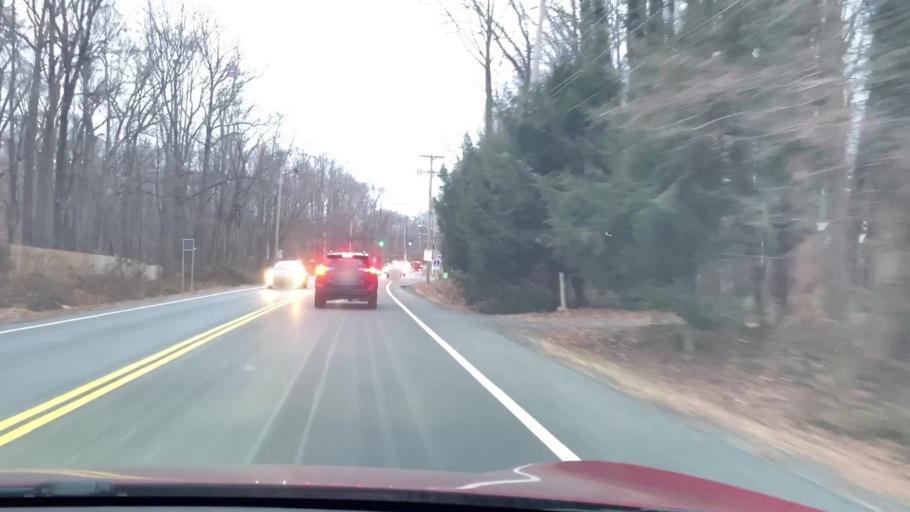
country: US
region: New York
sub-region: Rockland County
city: Sparkill
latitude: 41.0102
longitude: -73.9134
